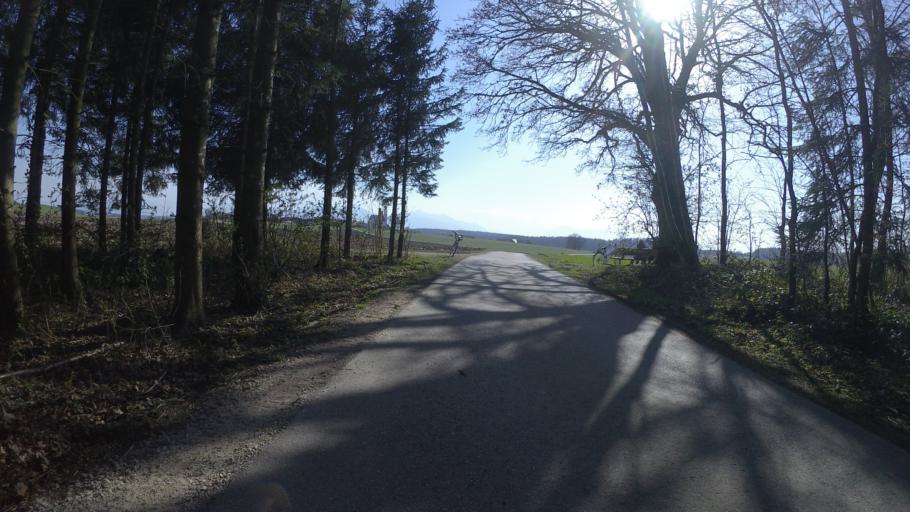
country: DE
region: Bavaria
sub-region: Upper Bavaria
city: Nussdorf
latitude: 47.9118
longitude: 12.5974
